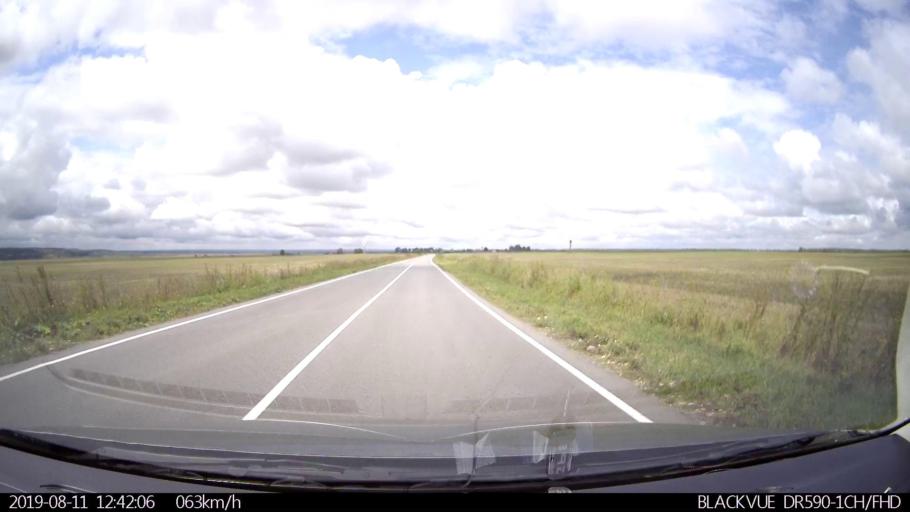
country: RU
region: Ulyanovsk
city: Ignatovka
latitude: 53.8434
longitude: 47.7554
